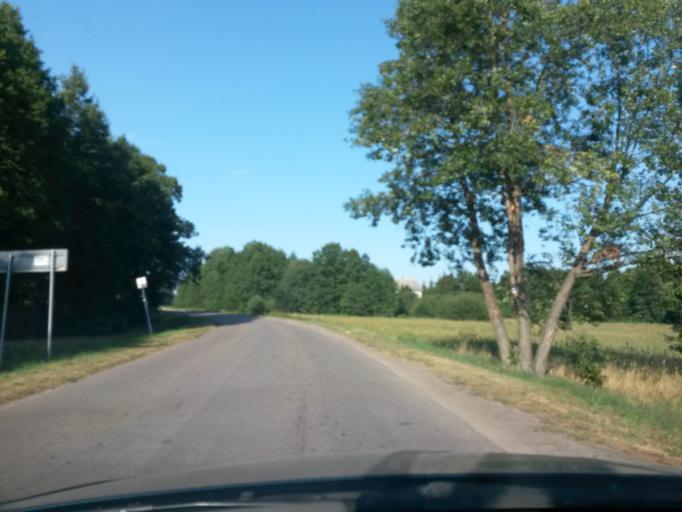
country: PL
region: Masovian Voivodeship
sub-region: Powiat sierpecki
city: Szczutowo
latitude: 52.9495
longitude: 19.5846
